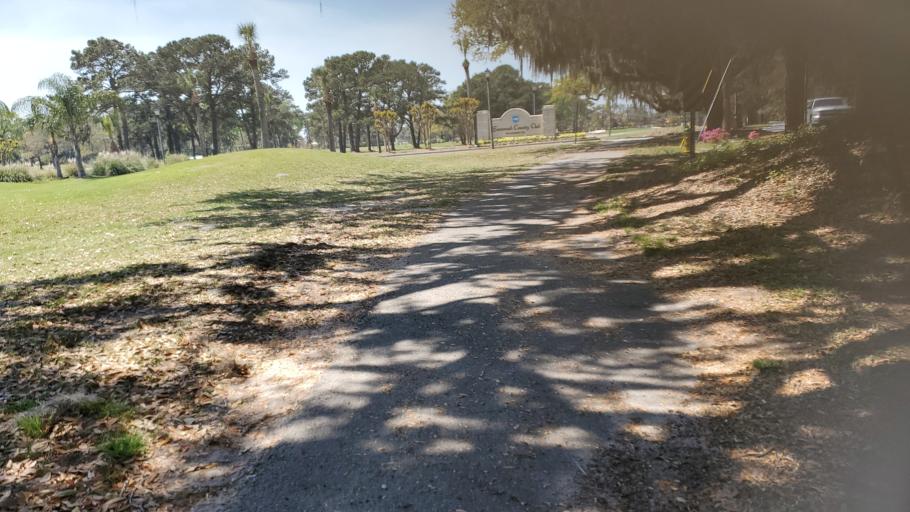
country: US
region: Georgia
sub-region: Chatham County
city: Wilmington Island
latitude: 32.0049
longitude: -80.9935
